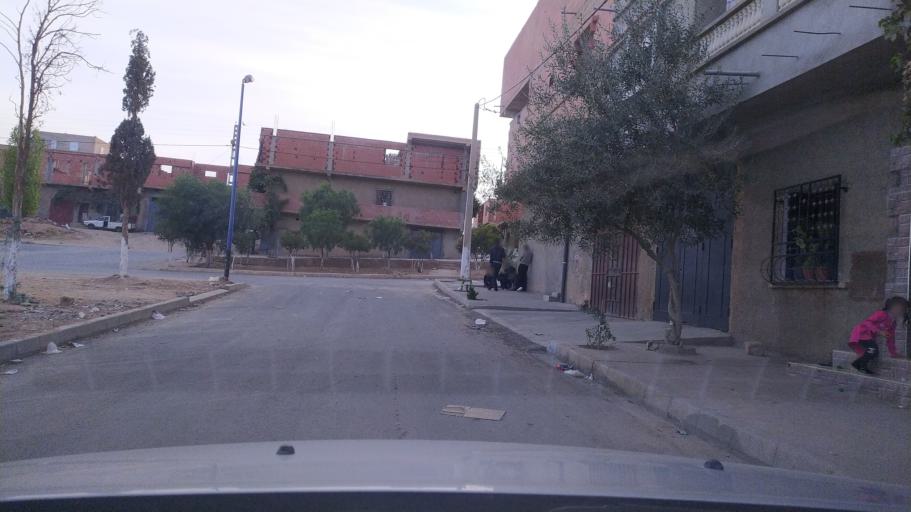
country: DZ
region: Tiaret
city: Frenda
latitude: 34.8951
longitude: 1.2395
